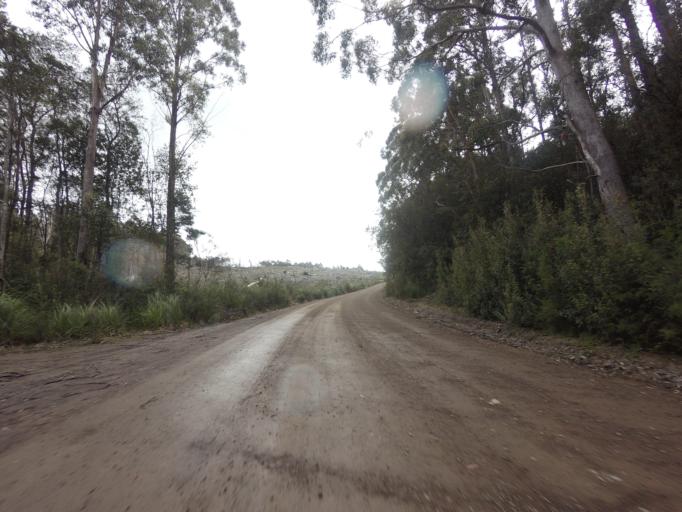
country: AU
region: Tasmania
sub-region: Huon Valley
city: Geeveston
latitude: -43.4905
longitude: 146.8873
